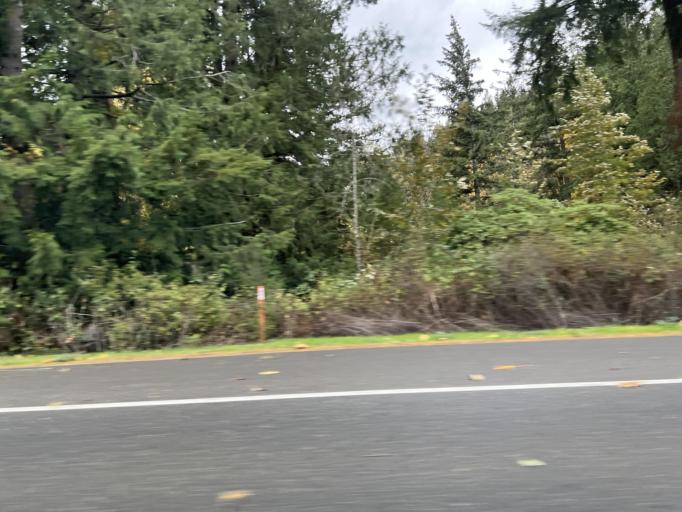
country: US
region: Washington
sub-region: King County
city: Tanner
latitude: 47.4875
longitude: -121.7578
